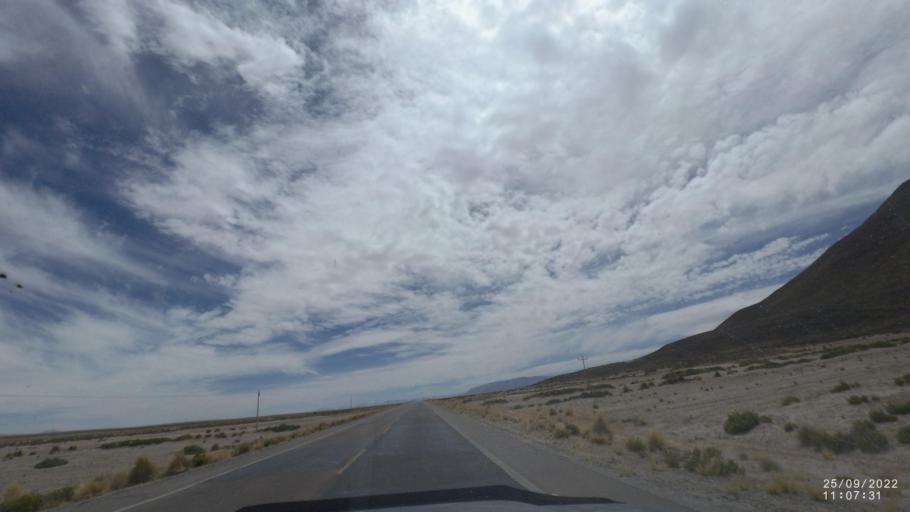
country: BO
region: Oruro
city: Challapata
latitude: -19.3426
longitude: -66.8545
